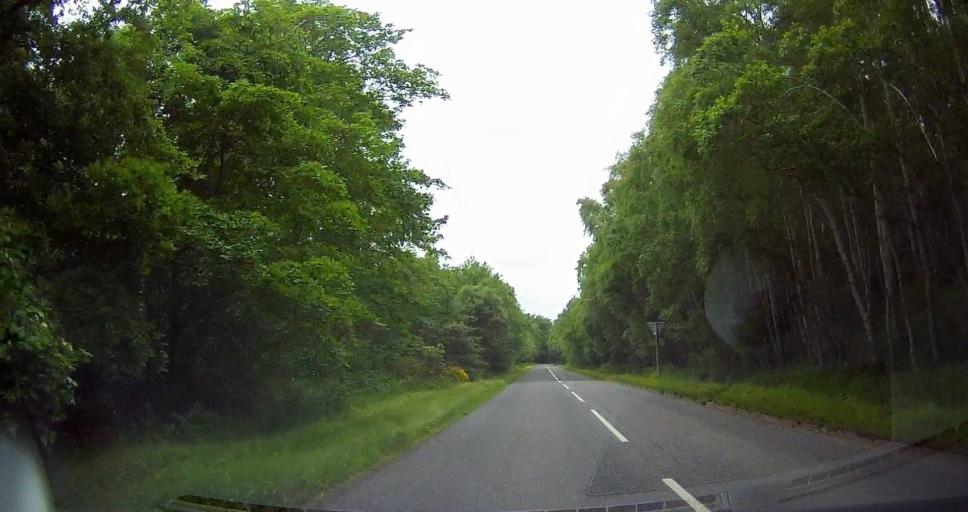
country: GB
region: Scotland
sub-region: Highland
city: Dornoch
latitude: 57.9585
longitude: -4.0700
